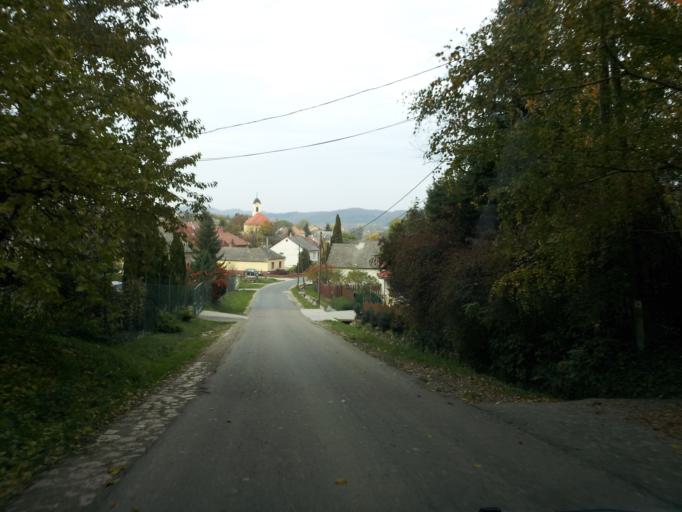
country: HU
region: Gyor-Moson-Sopron
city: Pannonhalma
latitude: 47.5087
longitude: 17.7501
